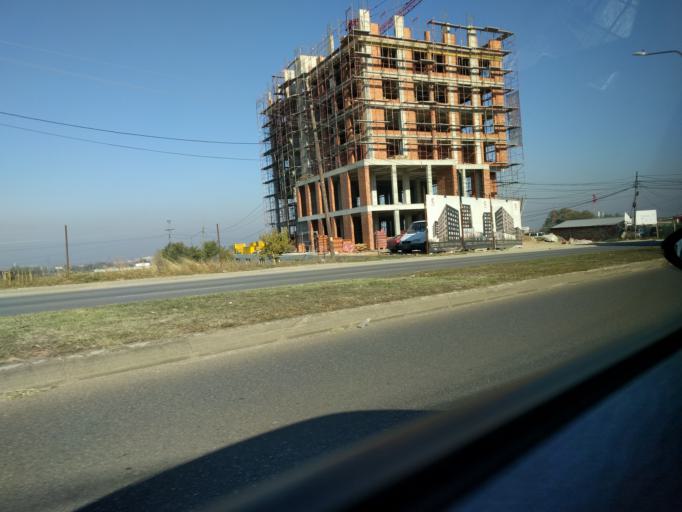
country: XK
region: Prizren
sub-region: Prizren
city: Prizren
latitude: 42.2290
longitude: 20.7543
